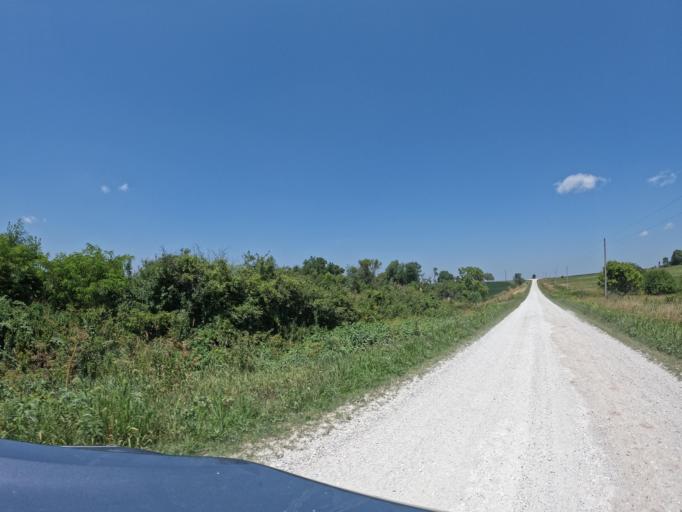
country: US
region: Iowa
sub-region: Keokuk County
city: Sigourney
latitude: 41.2720
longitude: -92.1701
